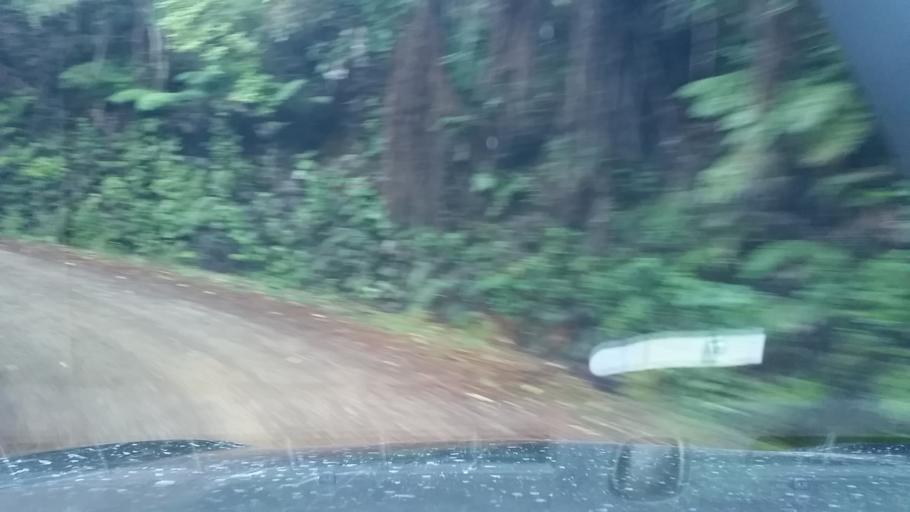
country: NZ
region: Marlborough
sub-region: Marlborough District
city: Picton
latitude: -41.1180
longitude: 173.9948
